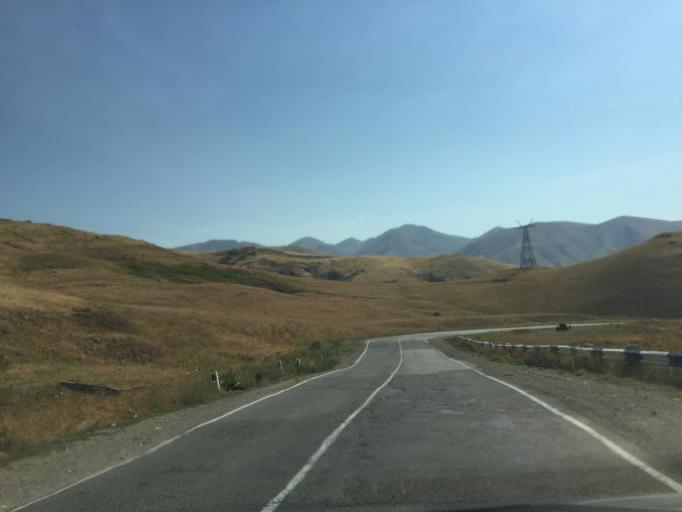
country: AM
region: Ararat
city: Zangakatun
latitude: 39.8197
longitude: 44.9996
